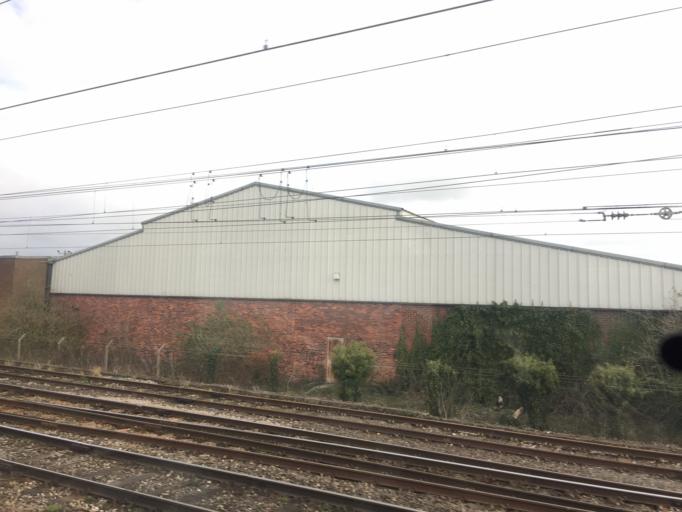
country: GB
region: England
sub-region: Cumbria
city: Carlisle
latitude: 54.8875
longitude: -2.9294
